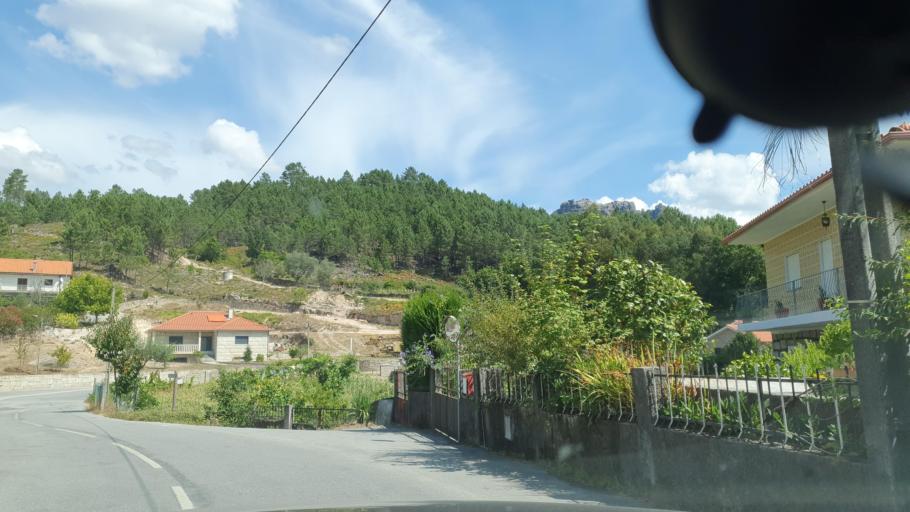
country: PT
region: Braga
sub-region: Vieira do Minho
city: Vieira do Minho
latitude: 41.7047
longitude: -8.0870
